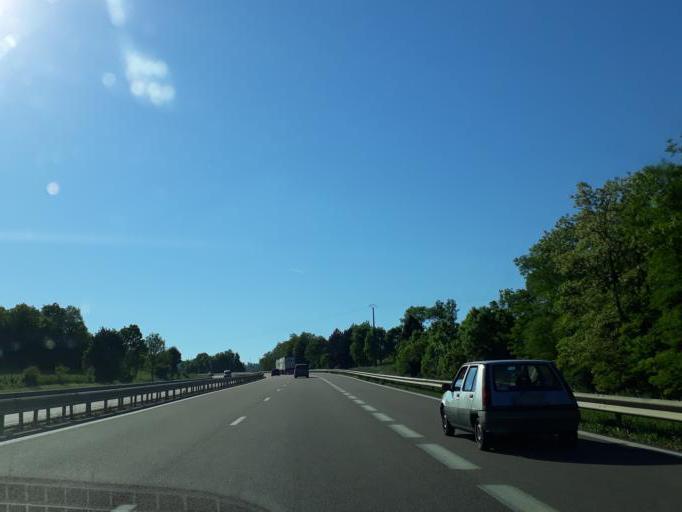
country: FR
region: Bourgogne
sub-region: Departement de la Cote-d'Or
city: Fleurey-sur-Ouche
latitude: 47.3063
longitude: 4.7467
